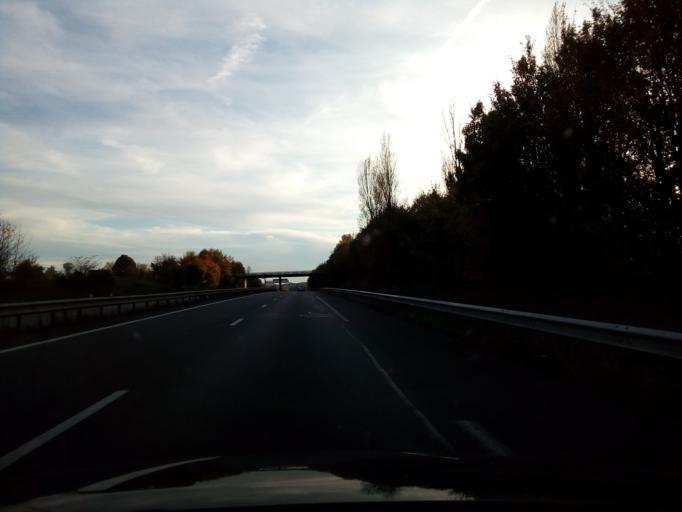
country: FR
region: Poitou-Charentes
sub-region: Departement de la Charente-Maritime
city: Chevanceaux
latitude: 45.3108
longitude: -0.2336
